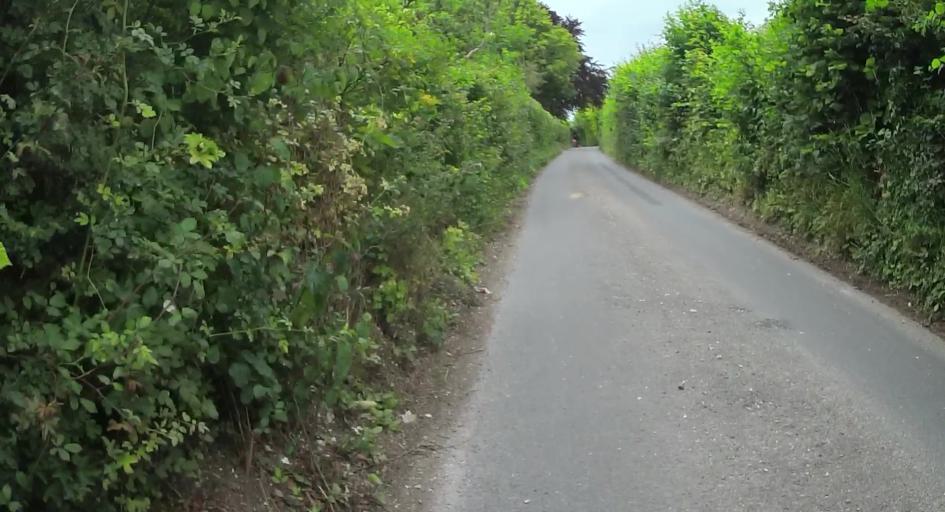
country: GB
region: England
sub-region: Hampshire
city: Four Marks
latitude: 51.0968
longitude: -1.1205
